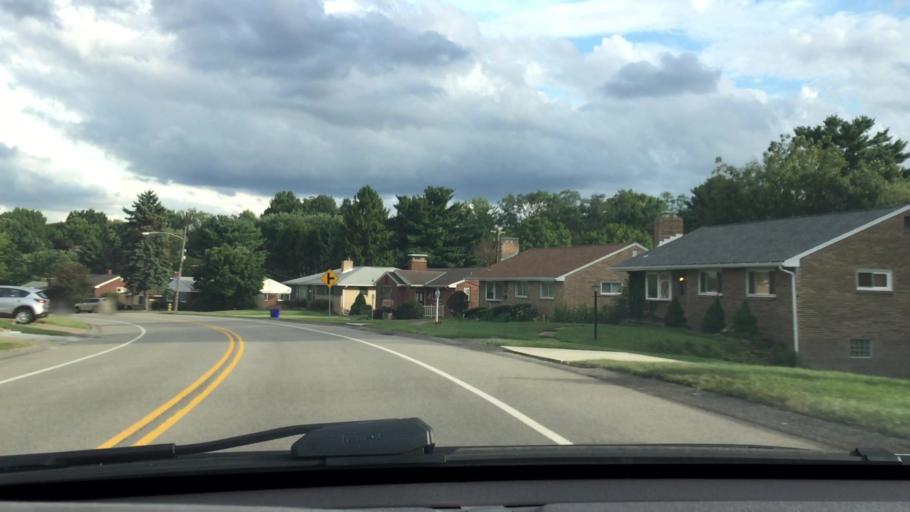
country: US
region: Pennsylvania
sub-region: Allegheny County
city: Green Tree
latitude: 40.4029
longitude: -80.0551
